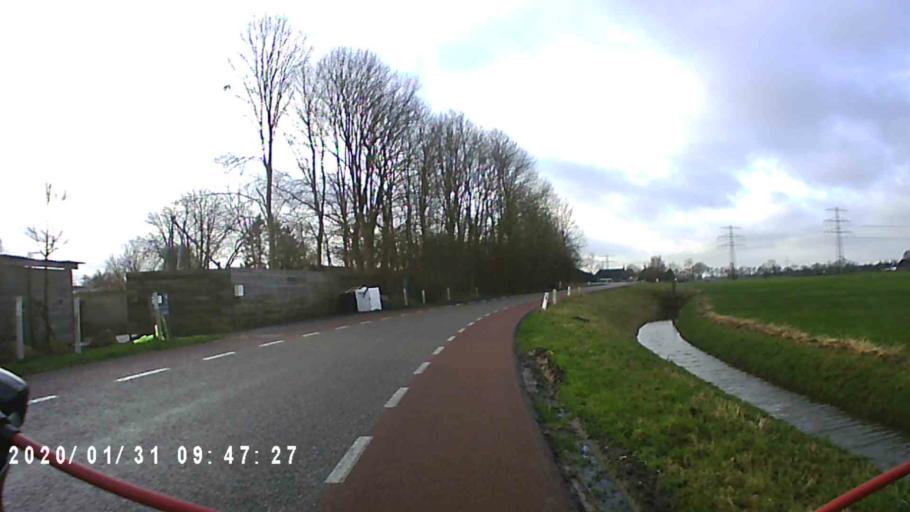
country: NL
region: Groningen
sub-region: Gemeente Zuidhorn
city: Aduard
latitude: 53.2631
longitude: 6.4825
